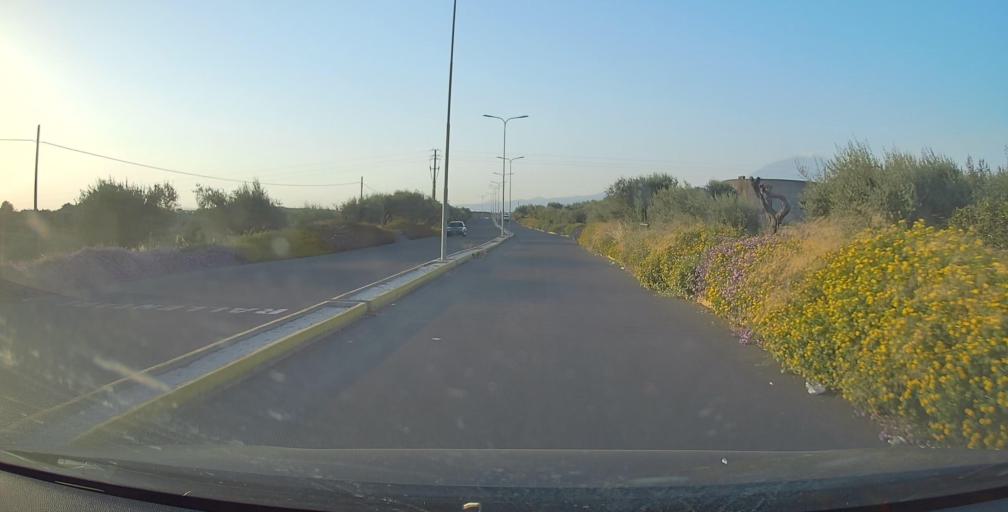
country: IT
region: Sicily
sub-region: Catania
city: Palazzolo
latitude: 37.5393
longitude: 14.9315
